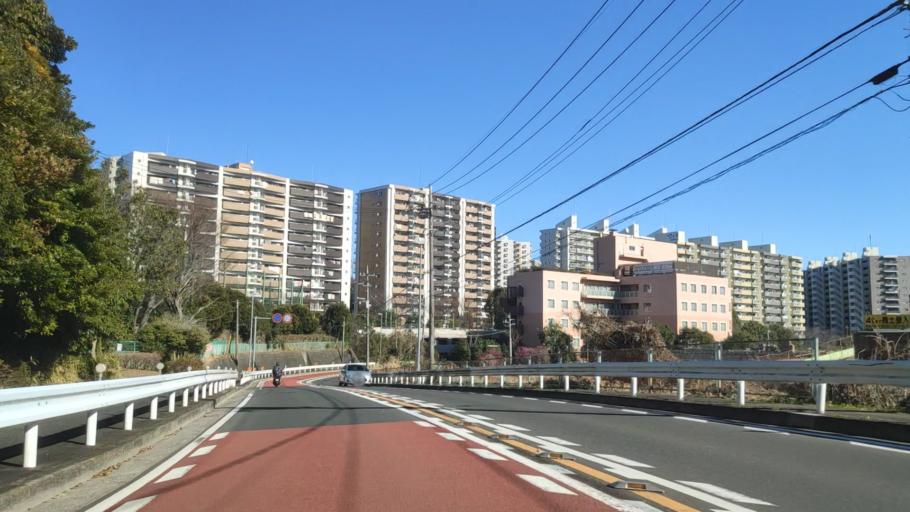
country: JP
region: Kanagawa
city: Minami-rinkan
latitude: 35.5041
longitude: 139.4920
